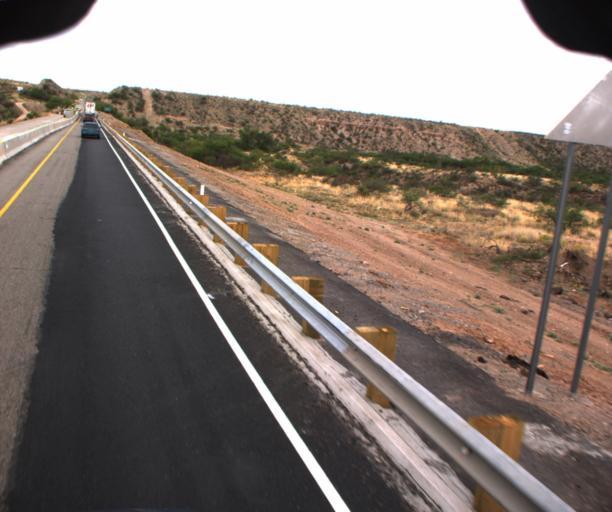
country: US
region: Arizona
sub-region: Pima County
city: Vail
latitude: 31.9979
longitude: -110.6433
